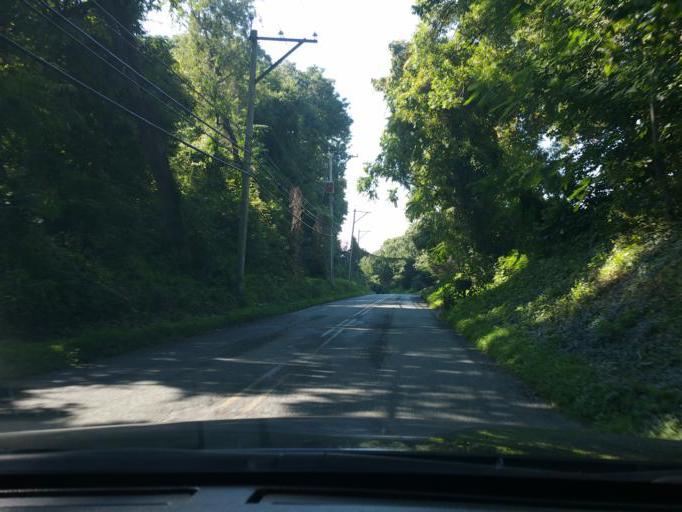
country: US
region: Maryland
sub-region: Cecil County
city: Rising Sun
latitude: 39.6715
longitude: -76.1555
